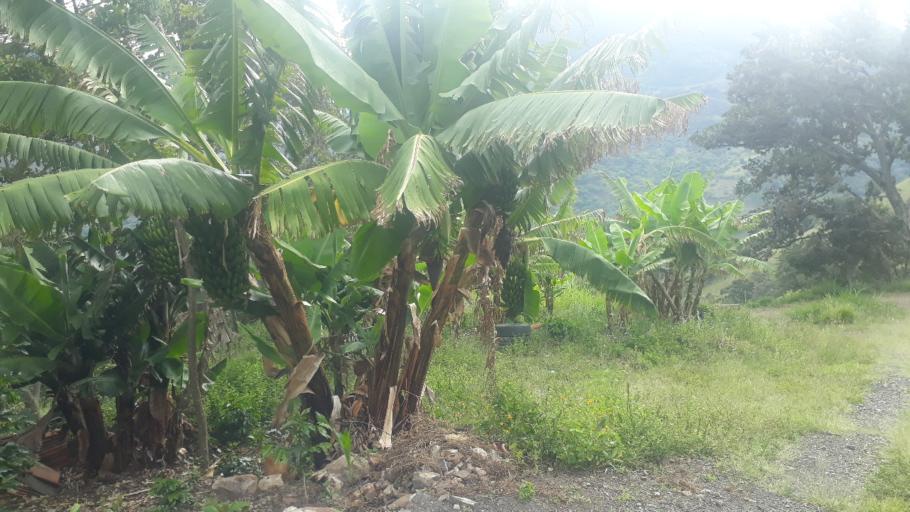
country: CO
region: Boyaca
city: San Mateo
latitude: 6.3942
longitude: -72.5830
